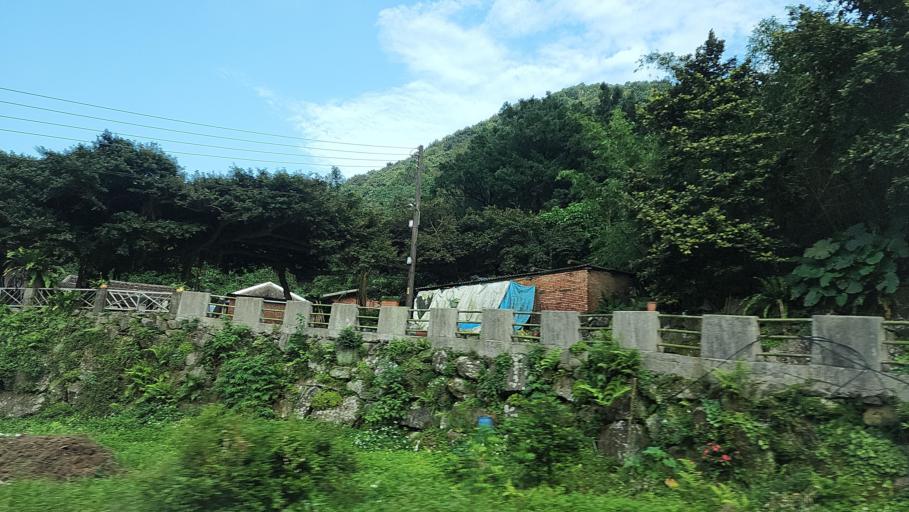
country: TW
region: Taiwan
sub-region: Keelung
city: Keelung
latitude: 25.1862
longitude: 121.6404
